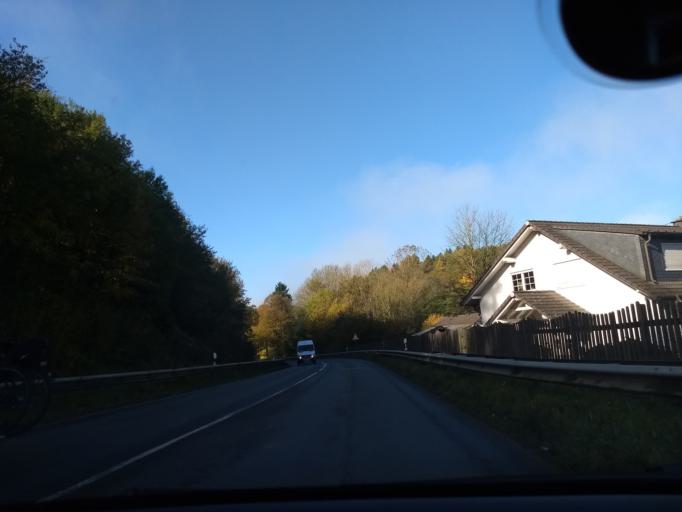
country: DE
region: North Rhine-Westphalia
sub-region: Regierungsbezirk Arnsberg
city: Finnentrop
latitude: 51.1806
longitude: 8.0168
